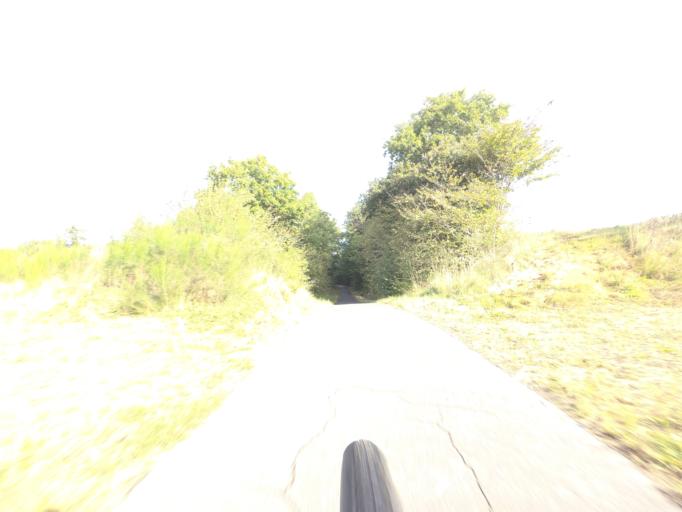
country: DK
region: Central Jutland
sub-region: Viborg Kommune
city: Bjerringbro
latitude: 56.4604
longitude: 9.5873
